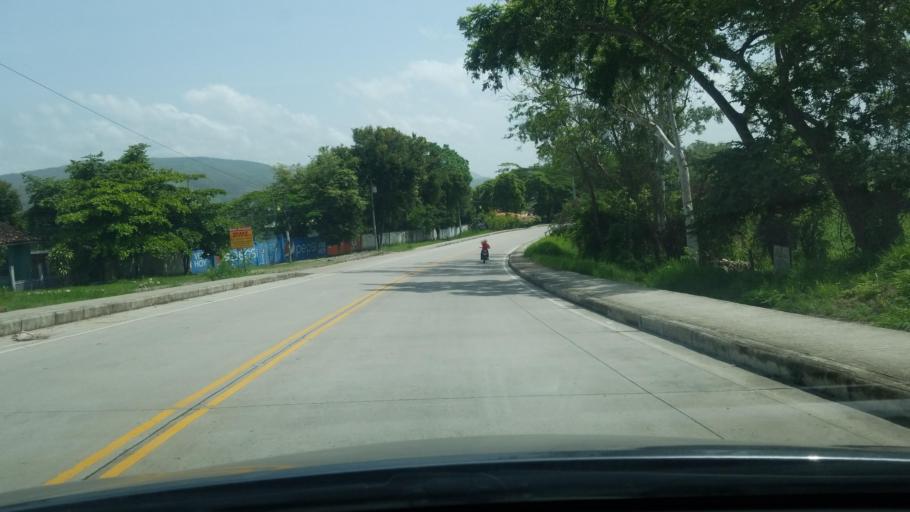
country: HN
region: Copan
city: Florida
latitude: 15.0280
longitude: -88.8319
